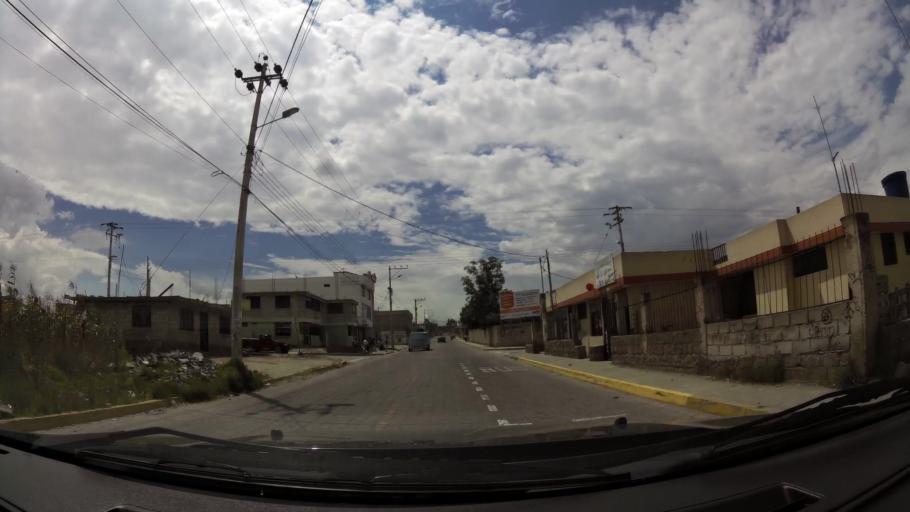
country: EC
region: Pichincha
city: Quito
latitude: -0.0679
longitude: -78.4147
